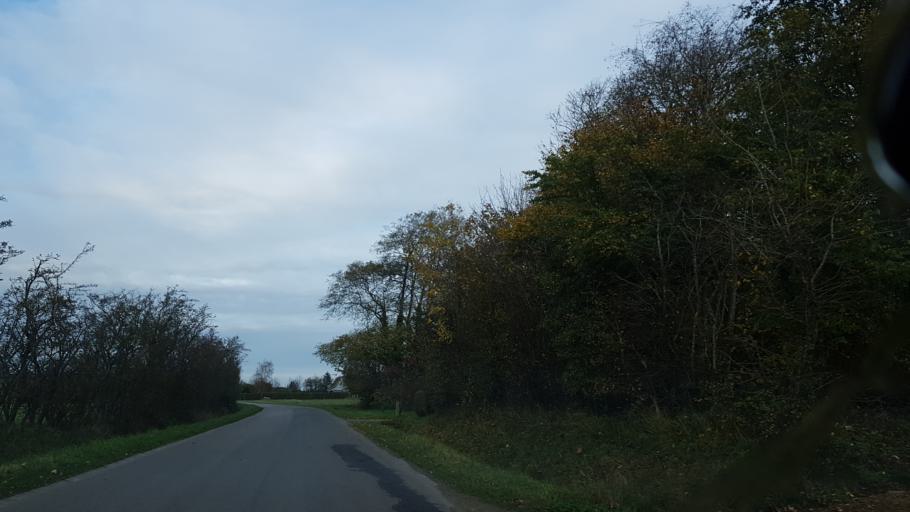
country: DK
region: South Denmark
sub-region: Haderslev Kommune
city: Vojens
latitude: 55.2537
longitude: 9.1925
